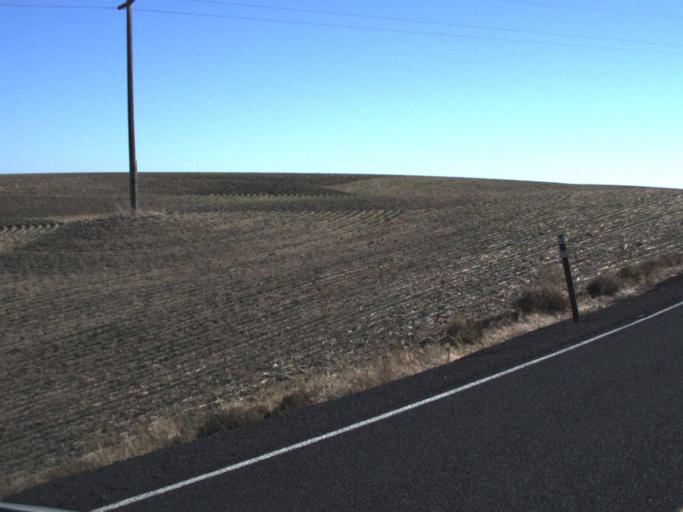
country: US
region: Washington
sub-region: Adams County
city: Ritzville
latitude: 46.8858
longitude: -118.5684
